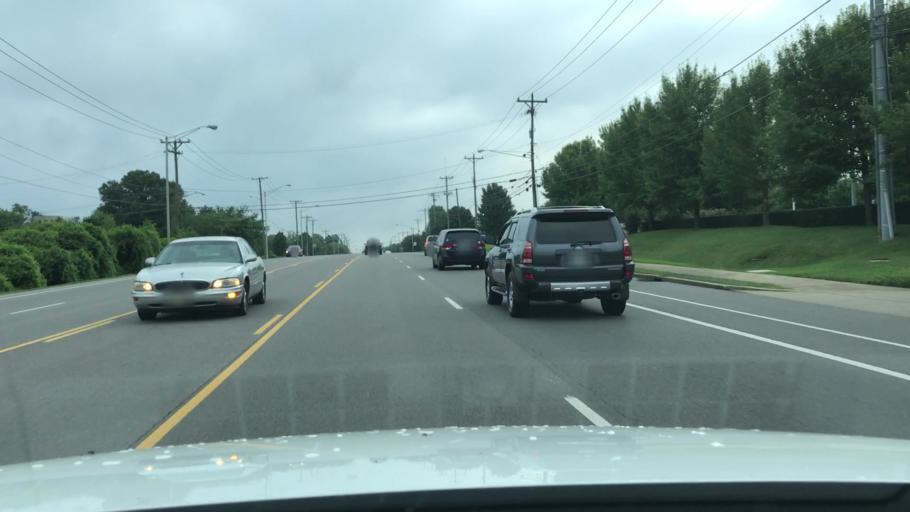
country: US
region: Tennessee
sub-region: Sumner County
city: Hendersonville
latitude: 36.3225
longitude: -86.5719
